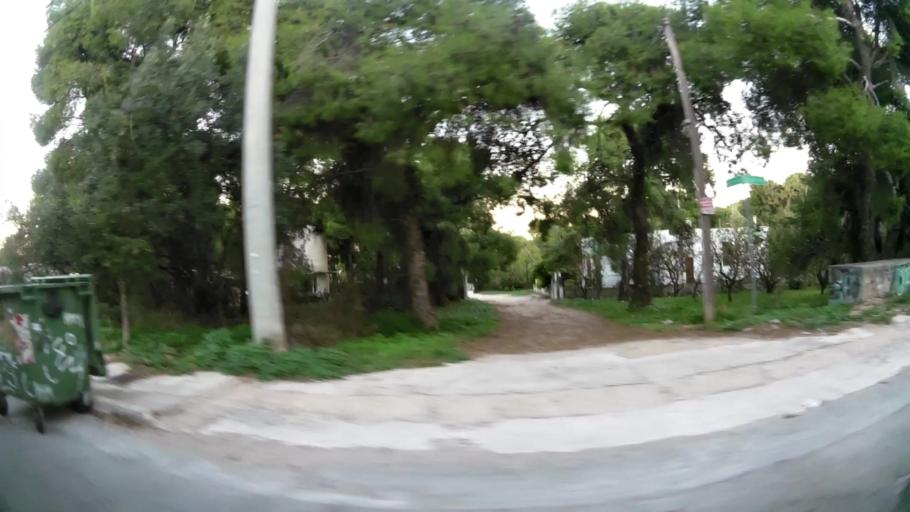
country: GR
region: Attica
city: Pefki
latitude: 38.0622
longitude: 23.7888
